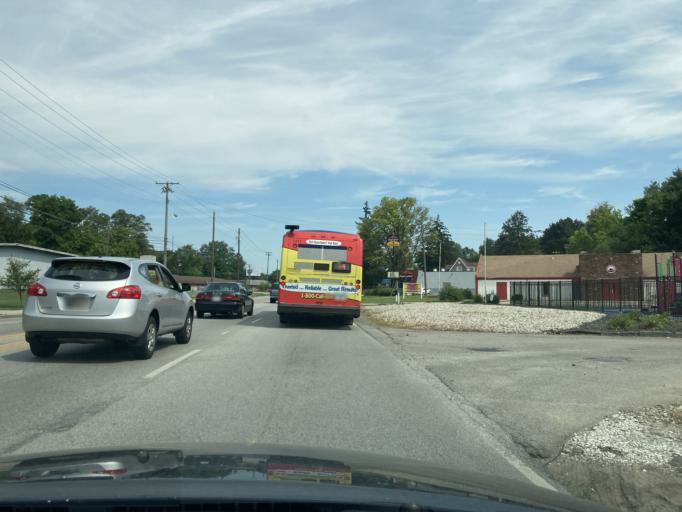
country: US
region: Indiana
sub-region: Marion County
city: Meridian Hills
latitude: 39.8579
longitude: -86.1967
